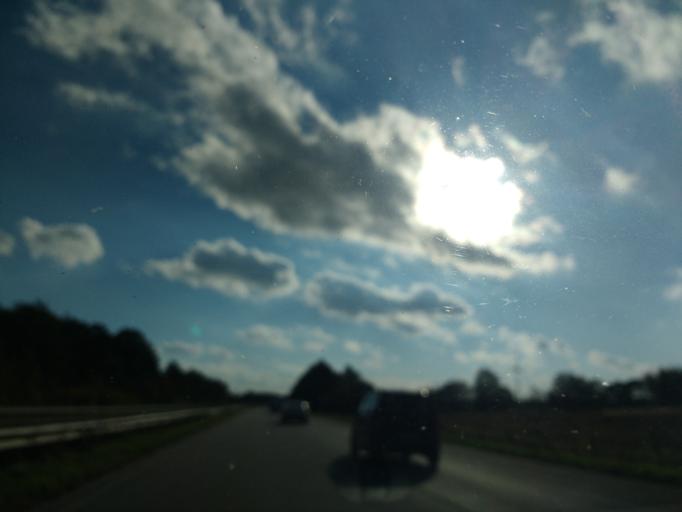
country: DE
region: Schleswig-Holstein
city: Travemuende
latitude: 53.9474
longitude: 10.8361
